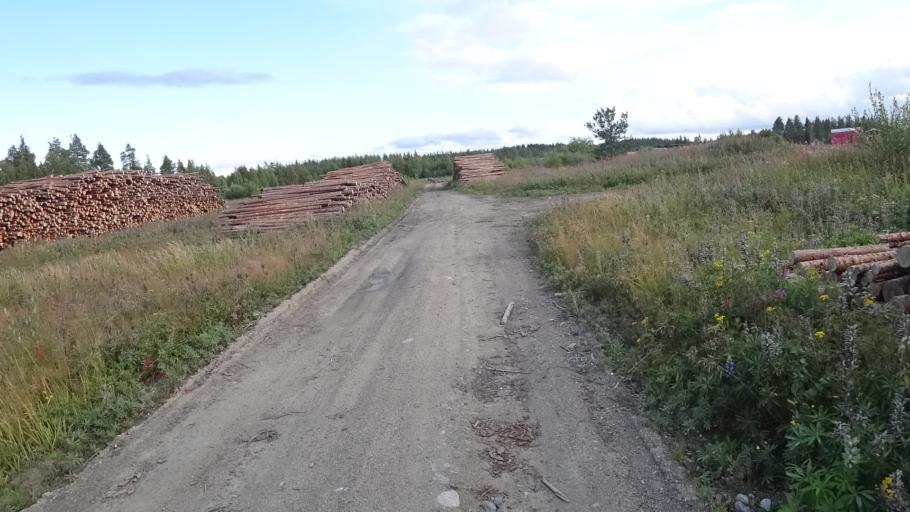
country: FI
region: North Karelia
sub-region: Joensuu
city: Ilomantsi
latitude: 62.6673
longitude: 30.9511
